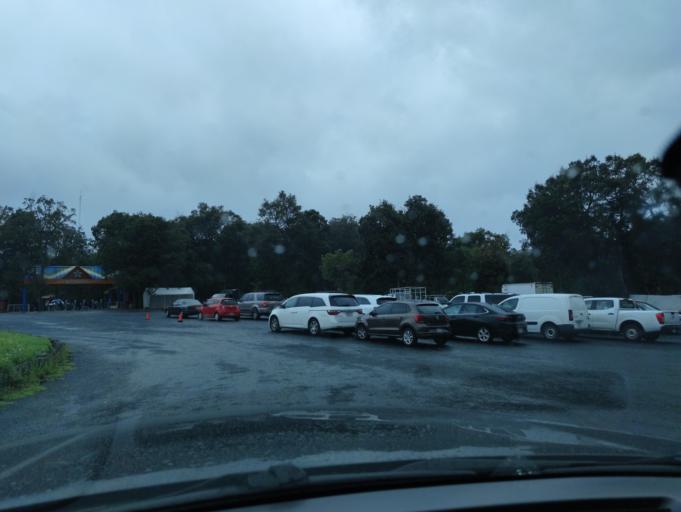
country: MX
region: Mexico
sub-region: Morelos
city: San Marcos Tlazalpan
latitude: 19.8724
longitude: -99.6609
